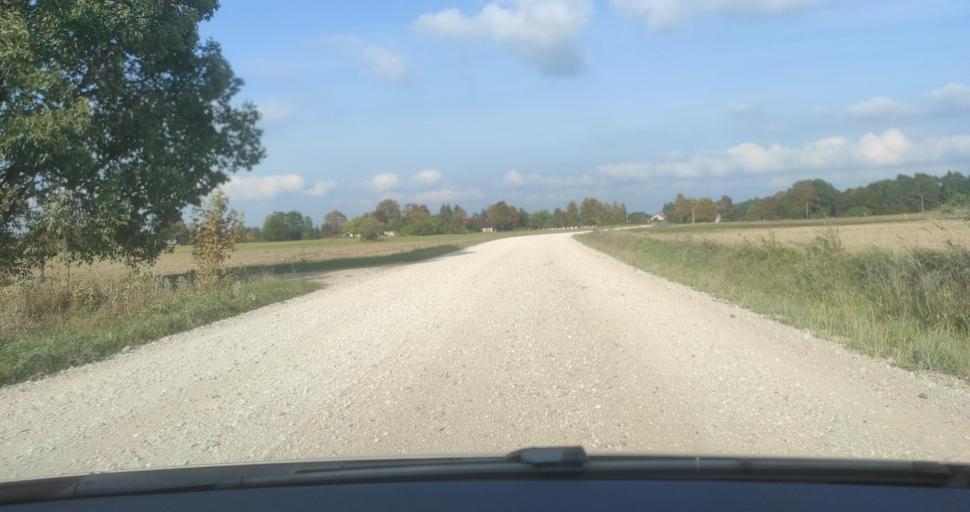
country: LV
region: Alsunga
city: Alsunga
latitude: 56.9937
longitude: 21.5816
